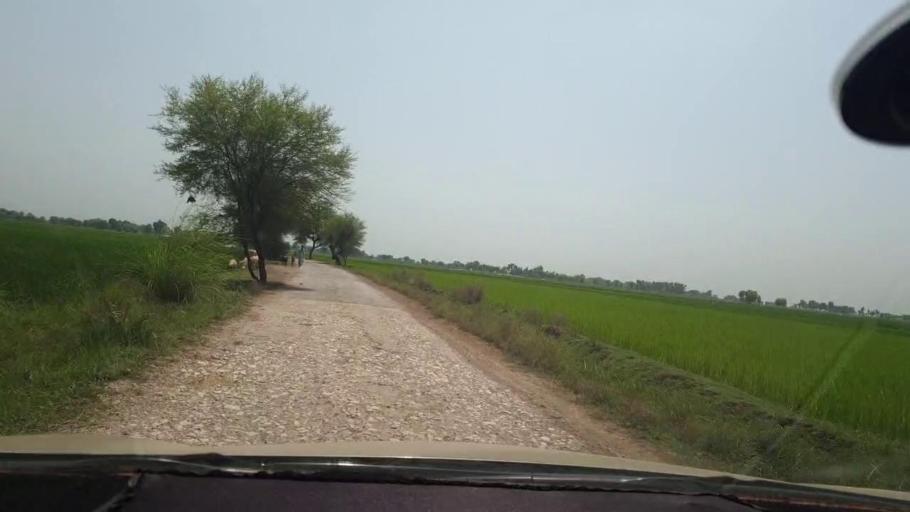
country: PK
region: Sindh
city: Kambar
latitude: 27.6444
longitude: 67.9320
